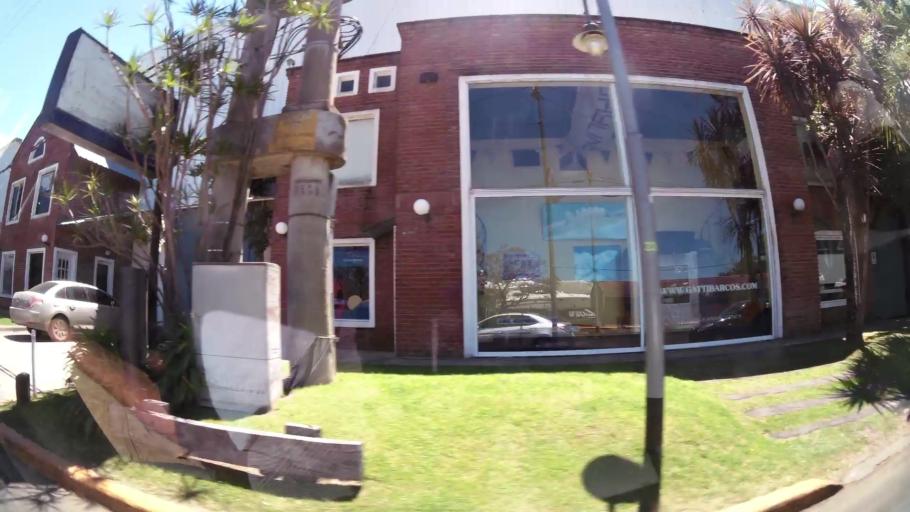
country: AR
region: Buenos Aires
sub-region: Partido de San Isidro
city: San Isidro
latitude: -34.4399
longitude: -58.5372
